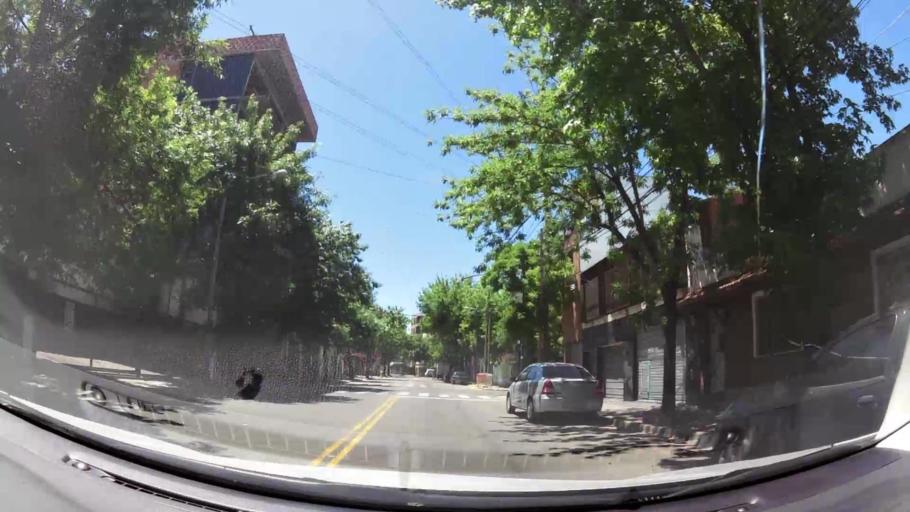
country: AR
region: Buenos Aires
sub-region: Partido de Tigre
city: Tigre
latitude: -34.4463
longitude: -58.5601
